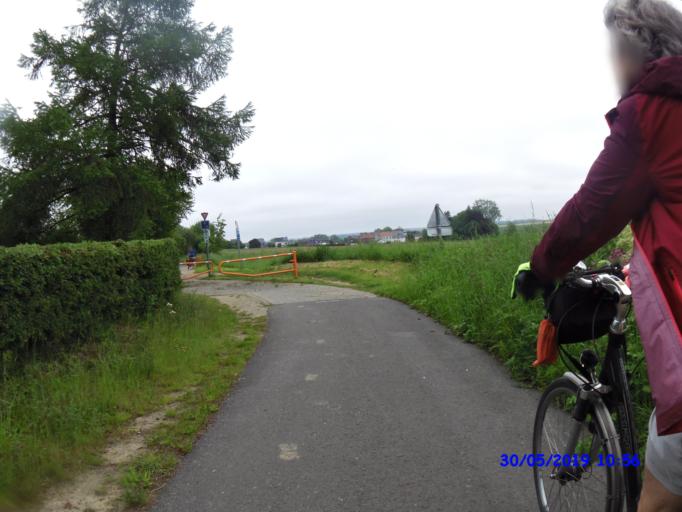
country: BE
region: Wallonia
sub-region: Province du Hainaut
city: Beaumont
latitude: 50.2680
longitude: 4.3000
